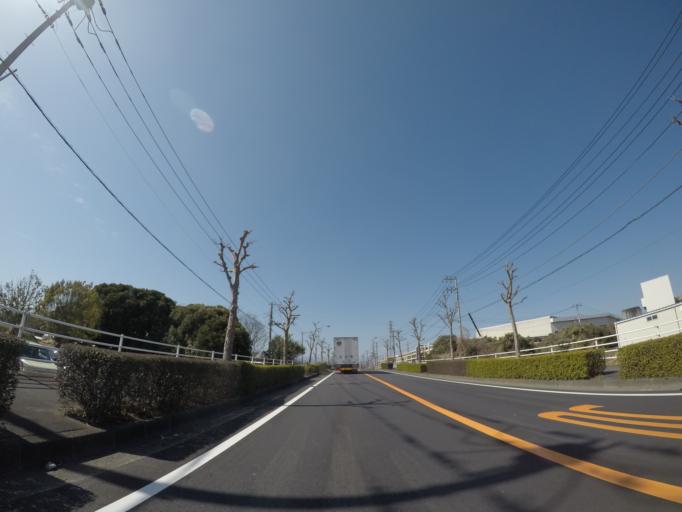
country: JP
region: Shizuoka
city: Fuji
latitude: 35.1598
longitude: 138.7112
